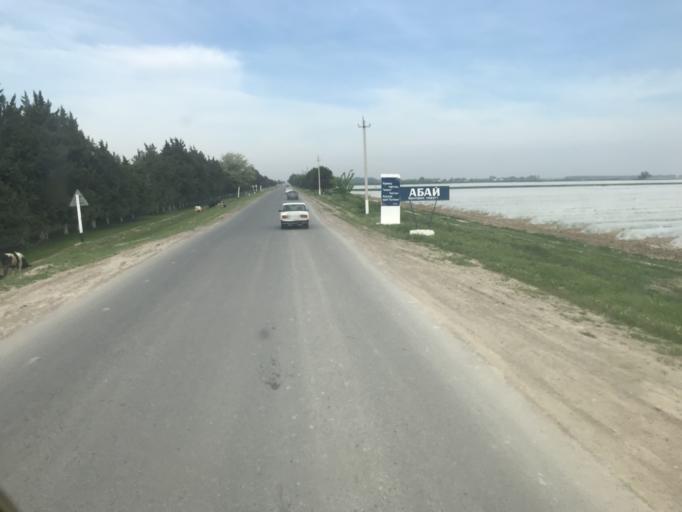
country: KZ
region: Ongtustik Qazaqstan
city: Asykata
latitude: 40.9843
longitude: 68.2959
